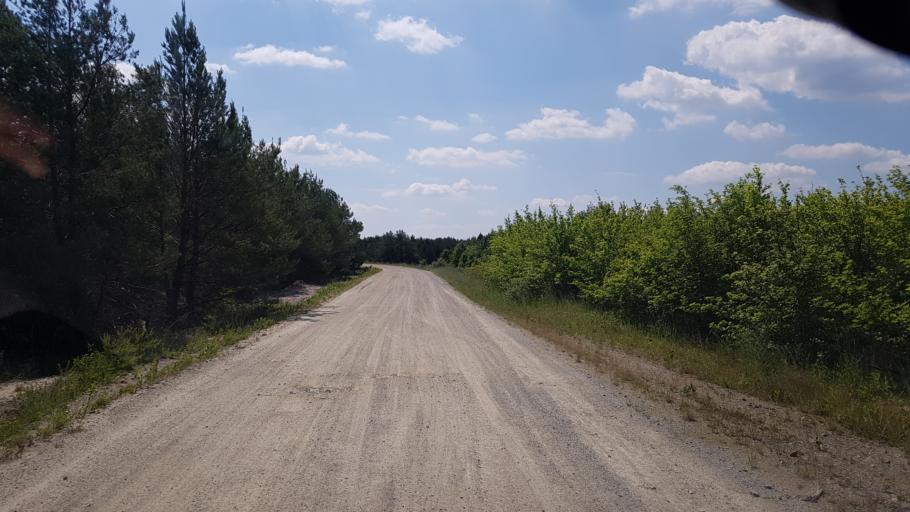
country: DE
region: Brandenburg
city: Lauchhammer
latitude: 51.5585
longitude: 13.7791
